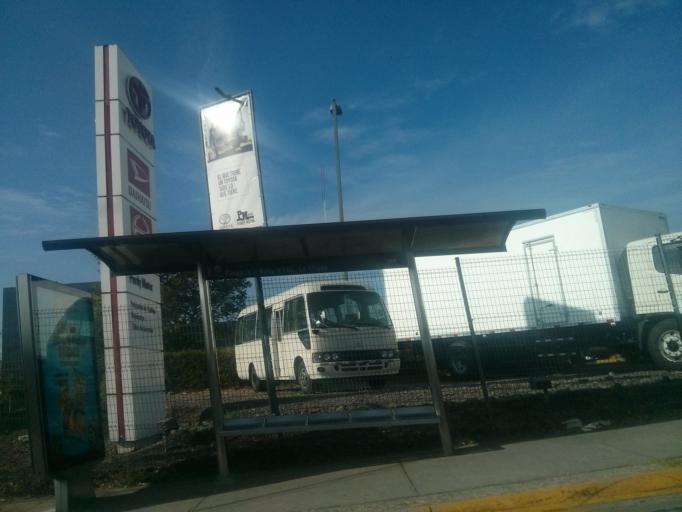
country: CR
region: San Jose
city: Colima
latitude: 9.9524
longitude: -84.1081
